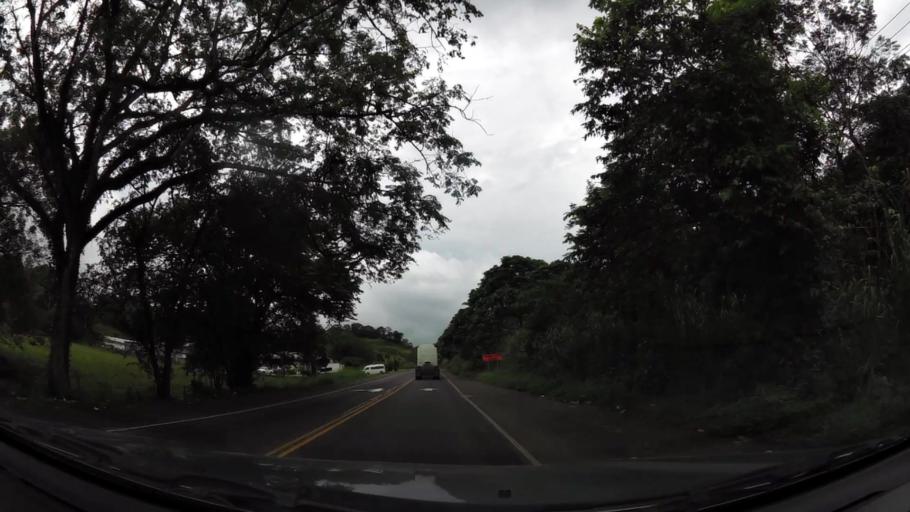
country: PA
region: Colon
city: Nuevo Vigia
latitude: 9.2166
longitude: -79.6262
